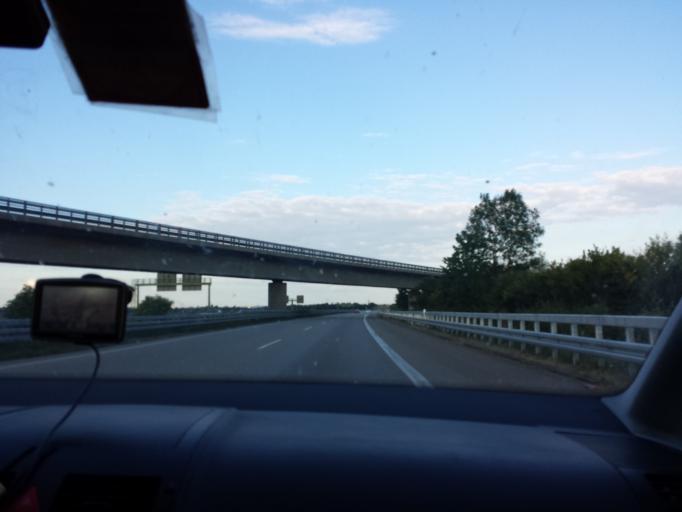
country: DE
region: Baden-Wuerttemberg
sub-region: Tuebingen Region
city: Langenau
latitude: 48.4651
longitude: 10.1132
